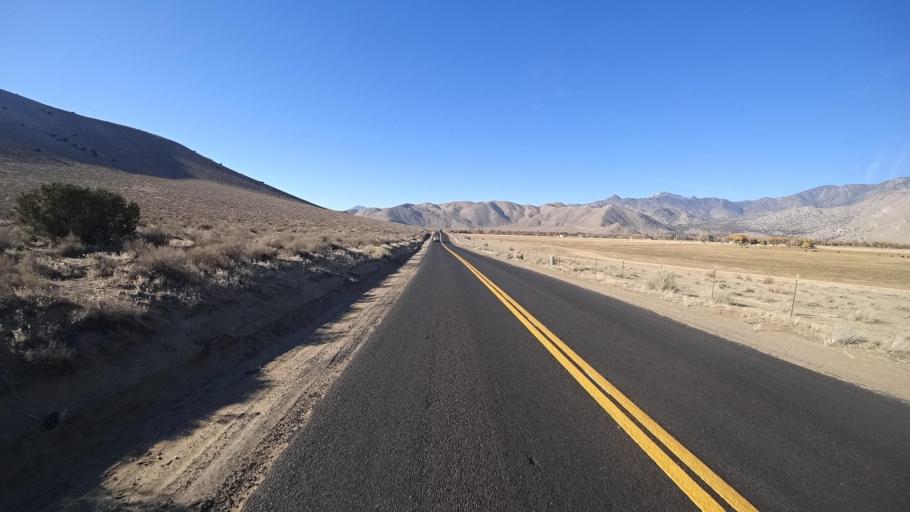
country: US
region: California
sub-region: Kern County
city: Weldon
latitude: 35.6573
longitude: -118.2886
